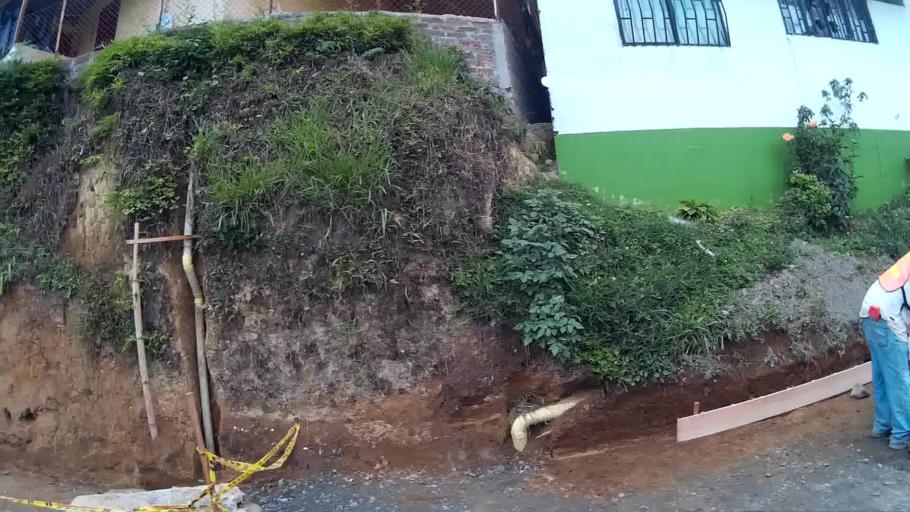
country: CO
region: Valle del Cauca
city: Ulloa
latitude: 4.7300
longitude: -75.7222
